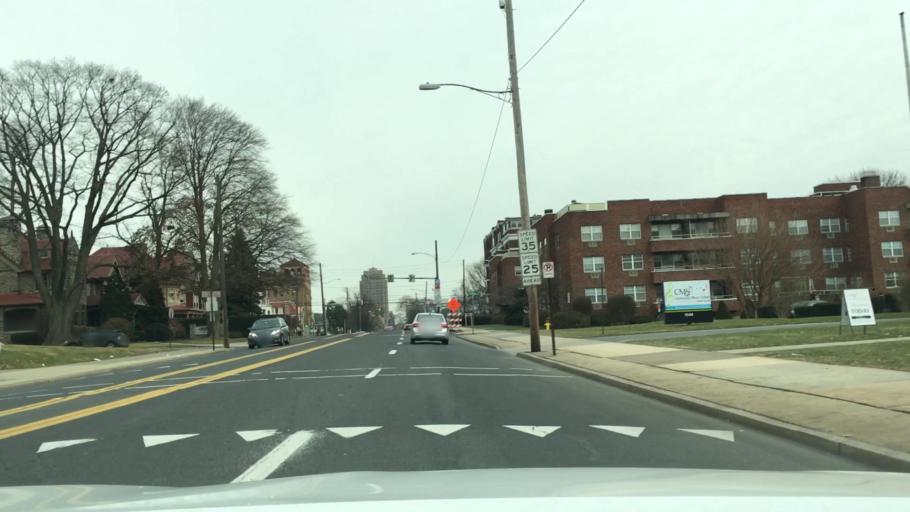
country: US
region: Pennsylvania
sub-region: Lehigh County
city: Allentown
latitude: 40.5972
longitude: -75.4898
